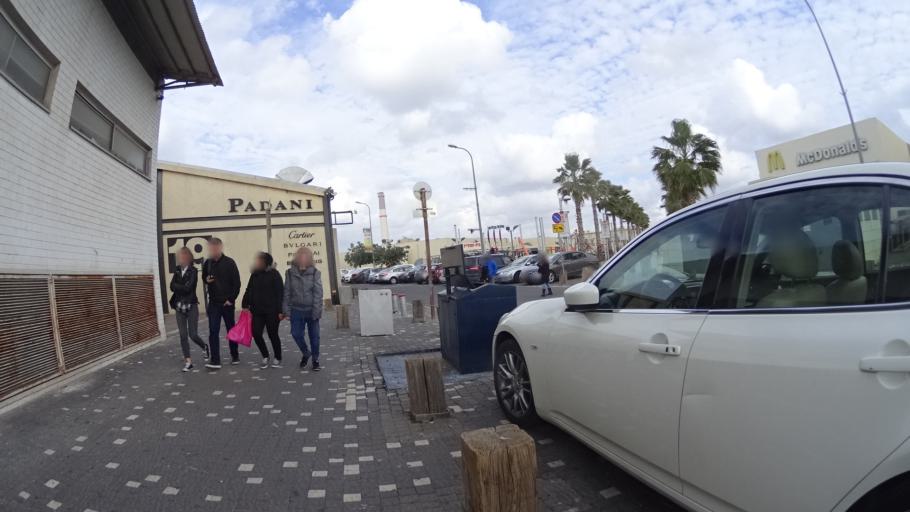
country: IL
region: Tel Aviv
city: Tel Aviv
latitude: 32.0990
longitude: 34.7743
